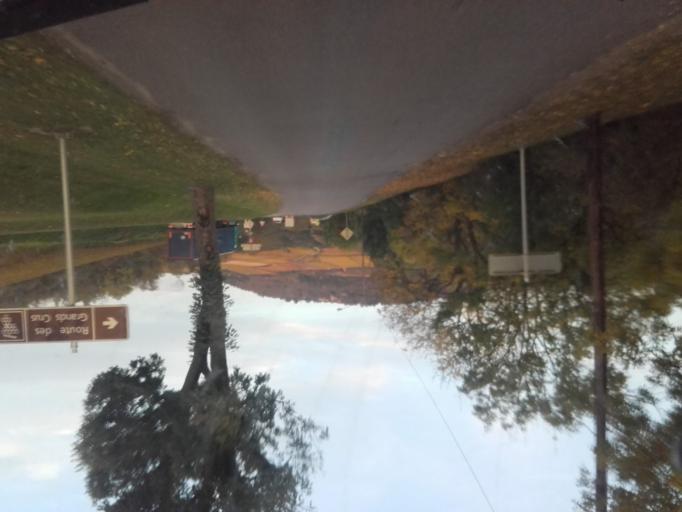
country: FR
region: Bourgogne
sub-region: Departement de la Cote-d'Or
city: Corpeau
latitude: 46.9525
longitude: 4.7162
